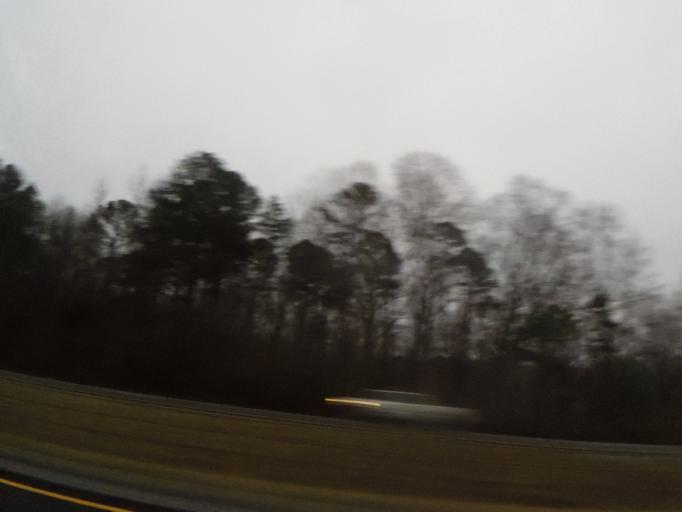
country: US
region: Alabama
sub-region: Cullman County
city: Cullman
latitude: 34.2347
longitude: -86.8808
